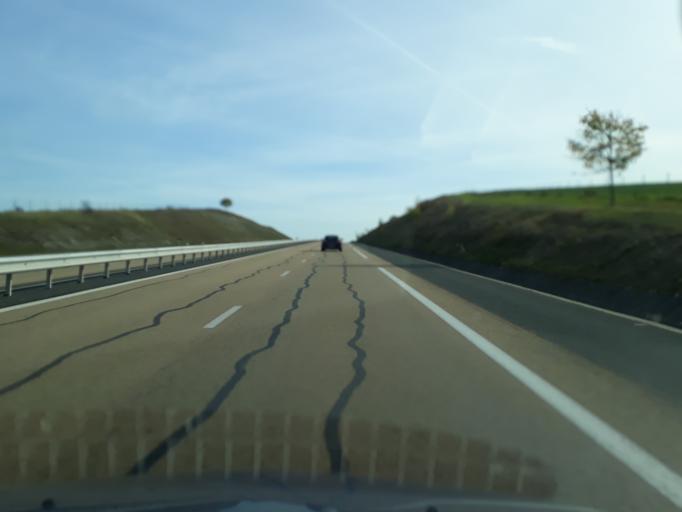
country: FR
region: Champagne-Ardenne
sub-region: Departement de l'Aube
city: Aix-en-Othe
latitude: 48.2689
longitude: 3.7238
